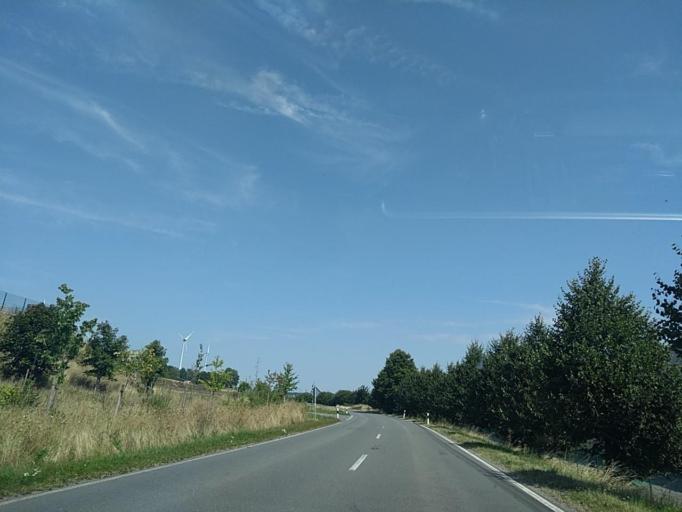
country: DE
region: North Rhine-Westphalia
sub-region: Regierungsbezirk Arnsberg
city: Brilon
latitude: 51.4101
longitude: 8.6005
